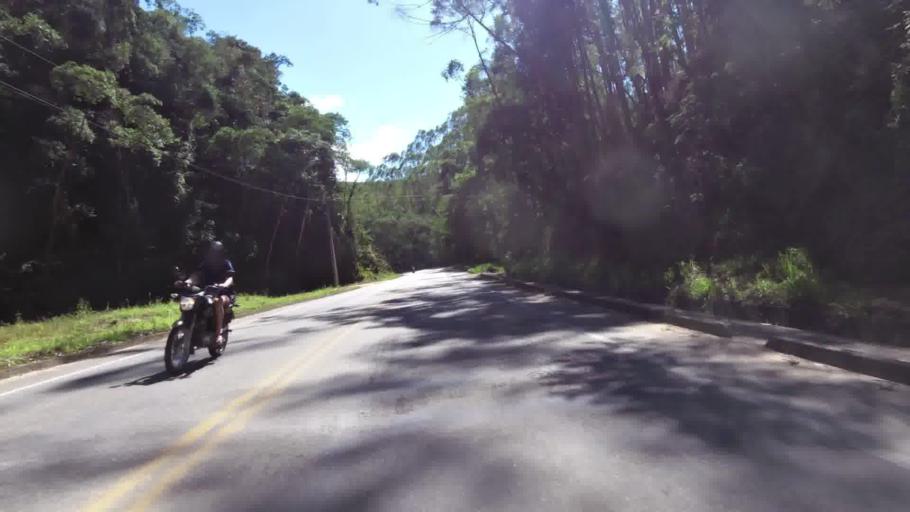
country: BR
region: Espirito Santo
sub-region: Vargem Alta
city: Vargem Alta
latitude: -20.6638
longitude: -40.9621
